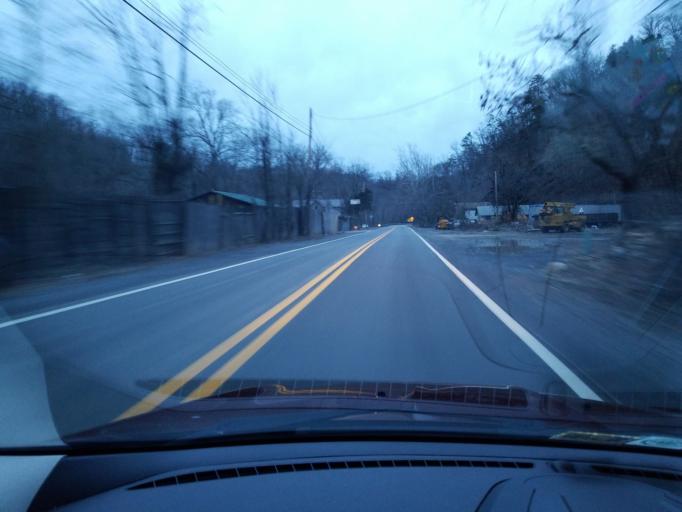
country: US
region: West Virginia
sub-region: Greenbrier County
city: Lewisburg
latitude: 37.7734
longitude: -80.3802
